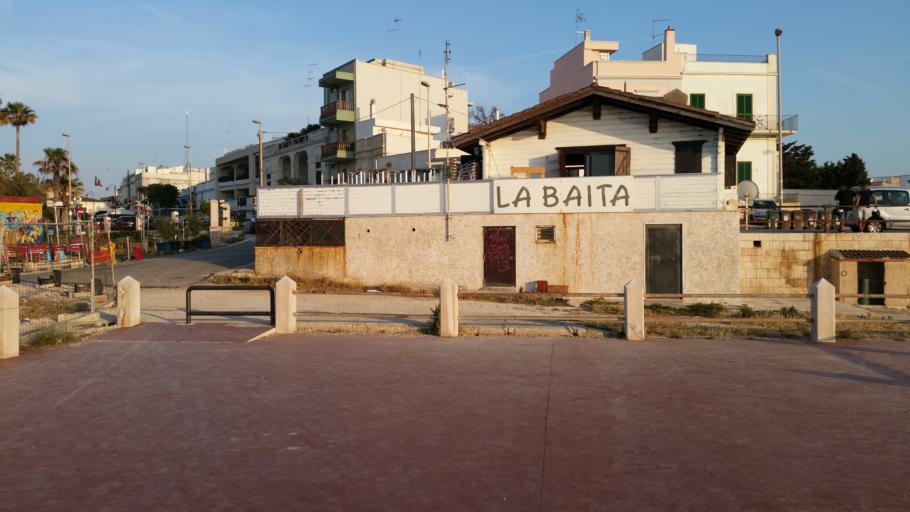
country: IT
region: Apulia
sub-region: Provincia di Bari
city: Parco Scizzo-Parchitello
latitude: 41.0884
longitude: 16.9981
